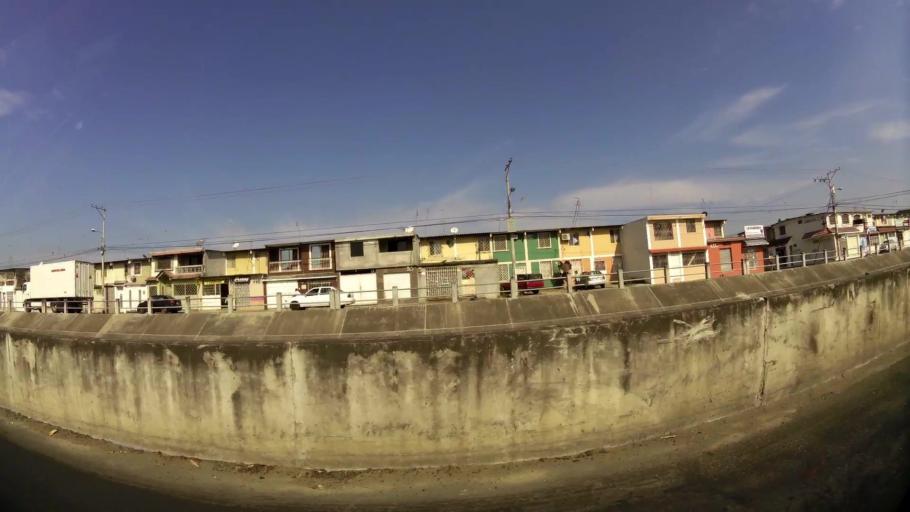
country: EC
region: Guayas
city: Eloy Alfaro
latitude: -2.0924
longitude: -79.9178
